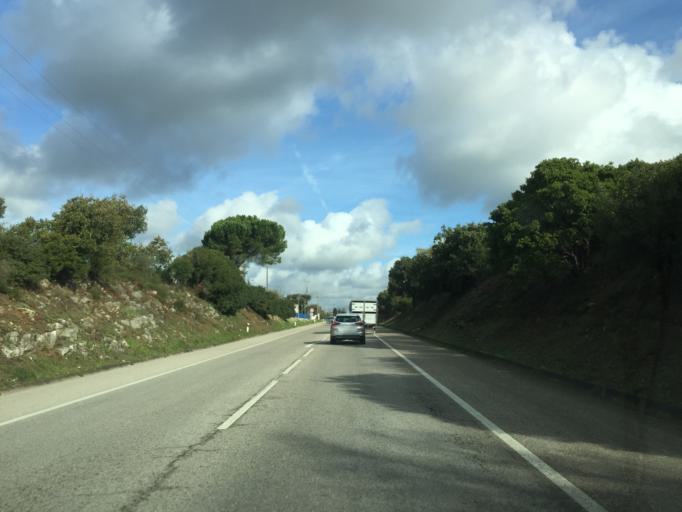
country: PT
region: Leiria
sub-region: Alcobaca
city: Aljubarrota
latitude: 39.5181
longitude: -8.9168
